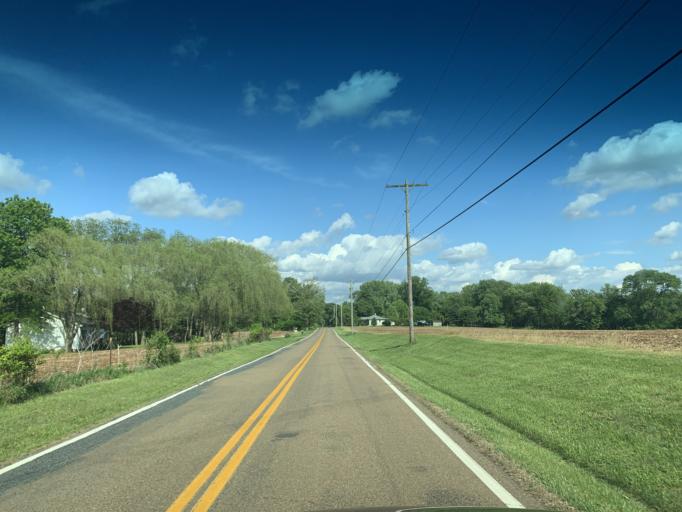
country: US
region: Maryland
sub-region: Cecil County
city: Rising Sun
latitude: 39.6980
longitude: -76.1654
